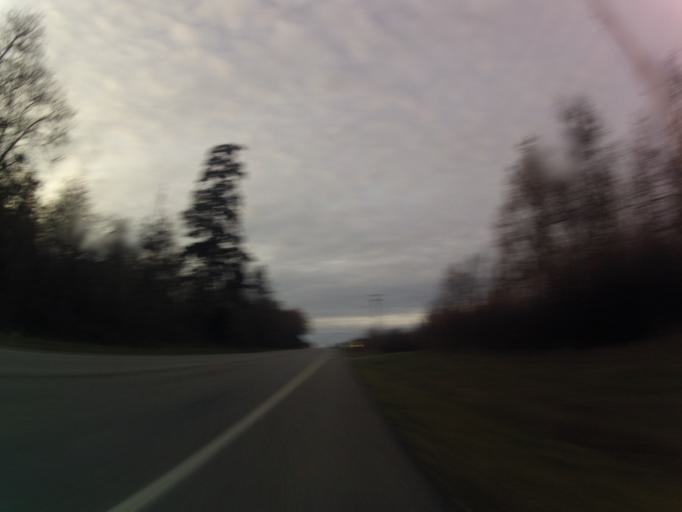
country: US
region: Washington
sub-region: Island County
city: Coupeville
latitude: 48.1716
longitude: -122.6795
